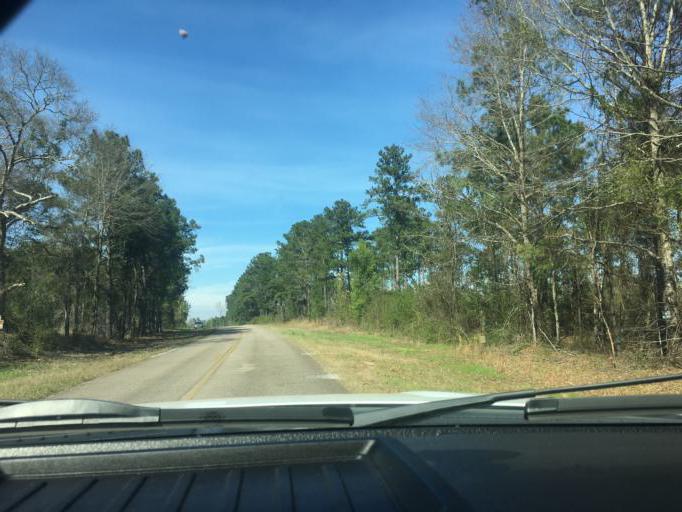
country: US
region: Alabama
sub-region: Lee County
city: Auburn
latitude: 32.4571
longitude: -85.4024
